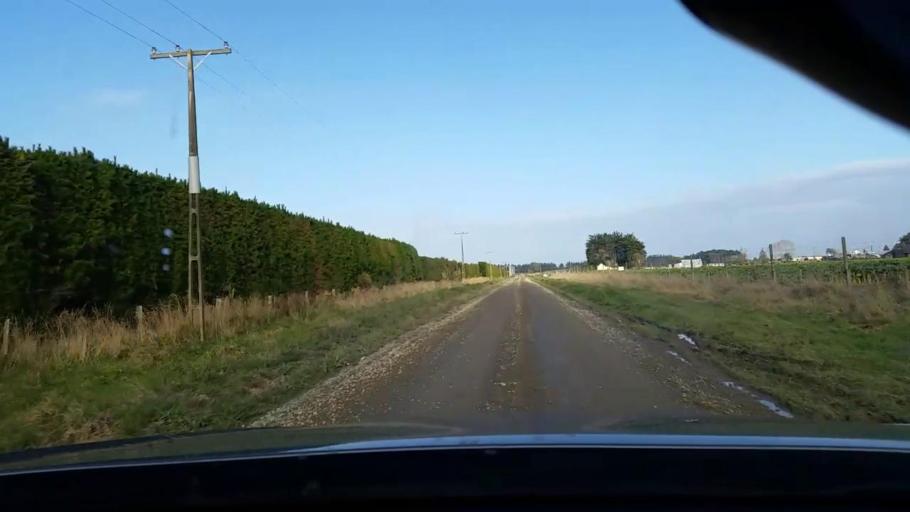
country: NZ
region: Southland
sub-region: Invercargill City
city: Invercargill
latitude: -46.2866
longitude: 168.2947
